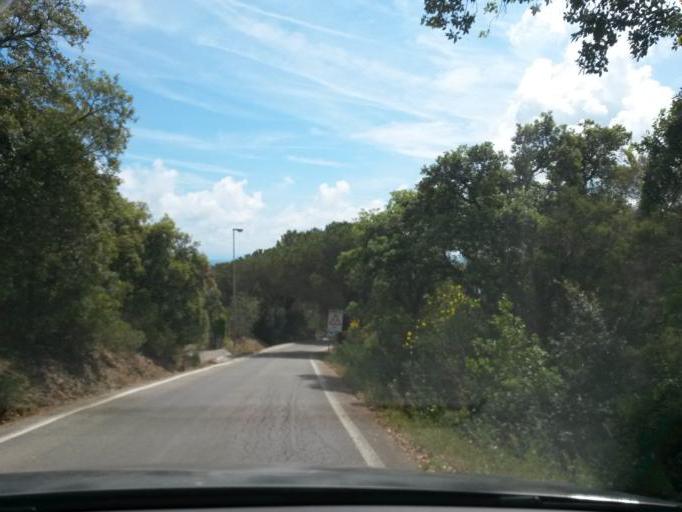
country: IT
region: Tuscany
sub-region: Provincia di Livorno
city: Porto Azzurro
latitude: 42.7567
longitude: 10.3993
